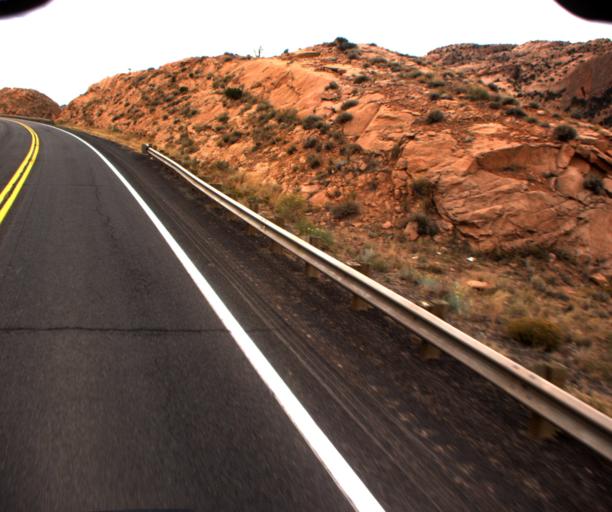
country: US
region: Arizona
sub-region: Navajo County
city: Kayenta
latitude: 36.6620
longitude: -110.4180
